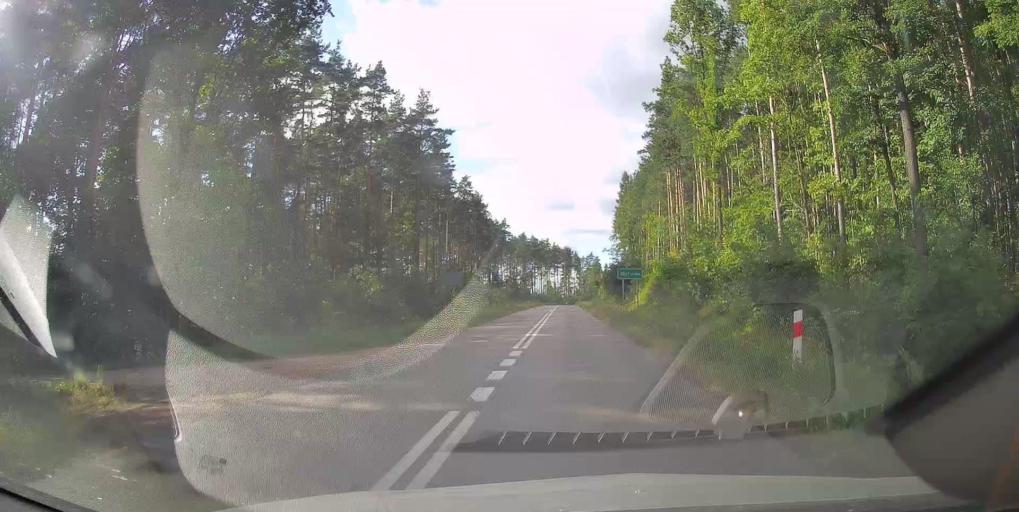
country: PL
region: Swietokrzyskie
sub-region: Powiat skarzyski
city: Suchedniow
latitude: 51.0108
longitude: 20.8418
